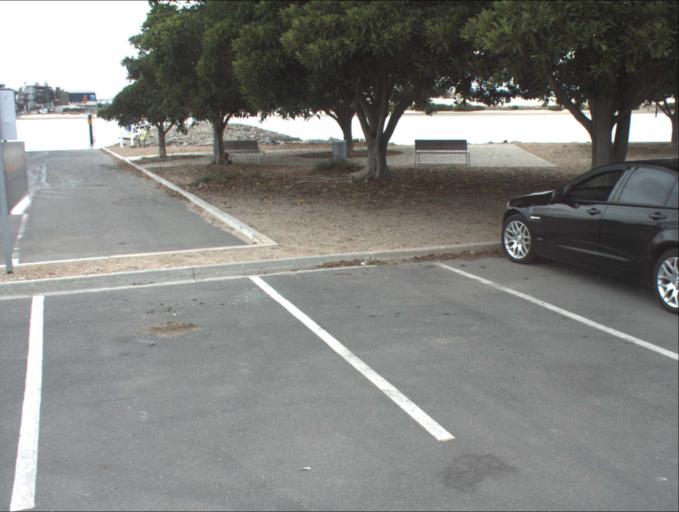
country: AU
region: South Australia
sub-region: Port Adelaide Enfield
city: Birkenhead
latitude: -34.8145
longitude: 138.5112
